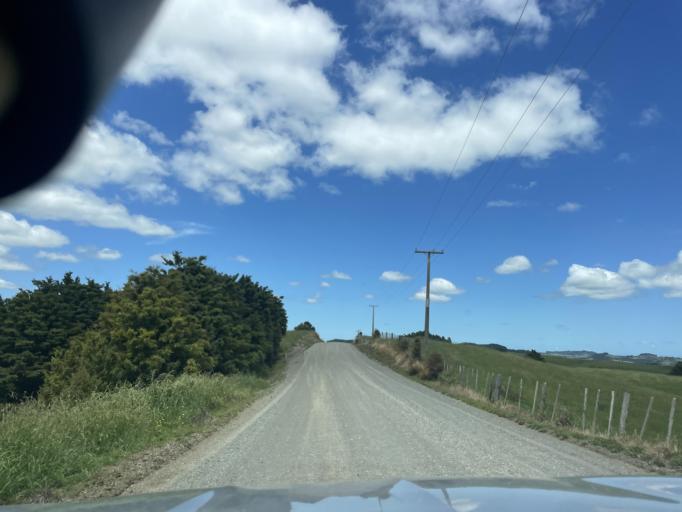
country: NZ
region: Auckland
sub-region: Auckland
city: Wellsford
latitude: -36.1581
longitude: 174.5386
